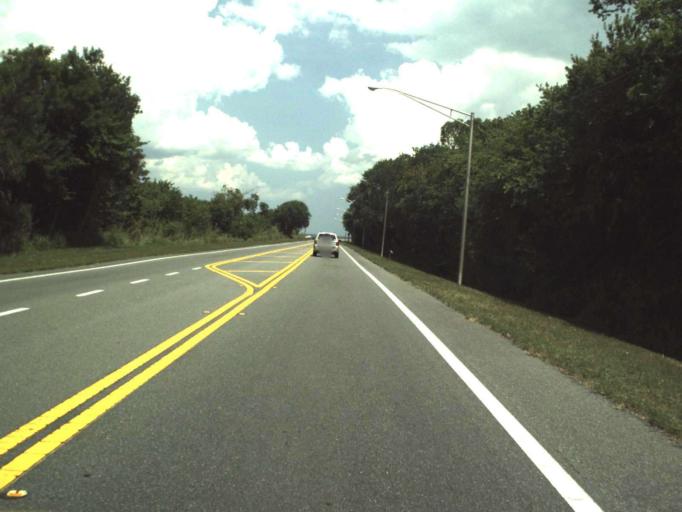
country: US
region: Florida
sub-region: Seminole County
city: Sanford
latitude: 28.8252
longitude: -81.3033
